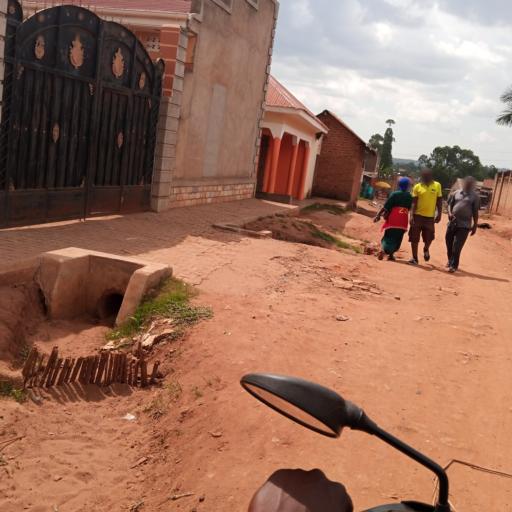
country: UG
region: Eastern Region
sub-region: Mbale District
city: Mbale
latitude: 1.0990
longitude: 34.1777
